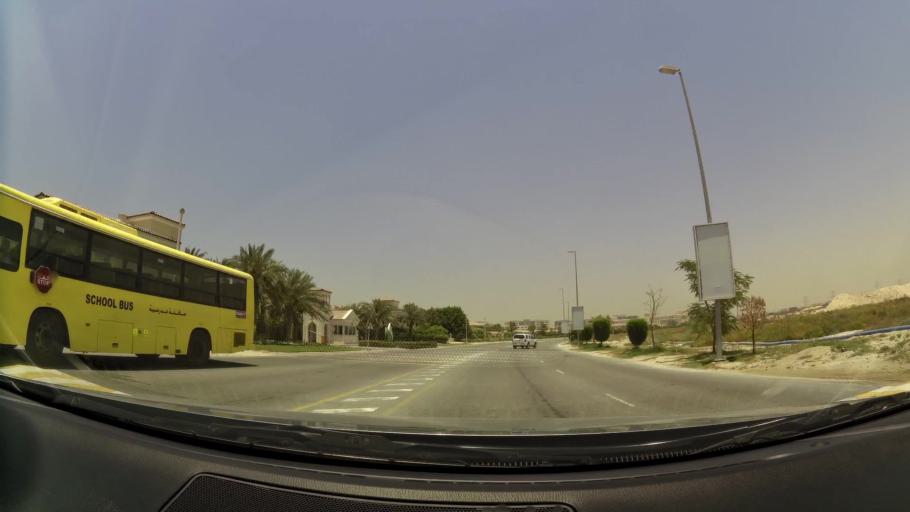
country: AE
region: Dubai
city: Dubai
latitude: 24.9927
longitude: 55.1672
